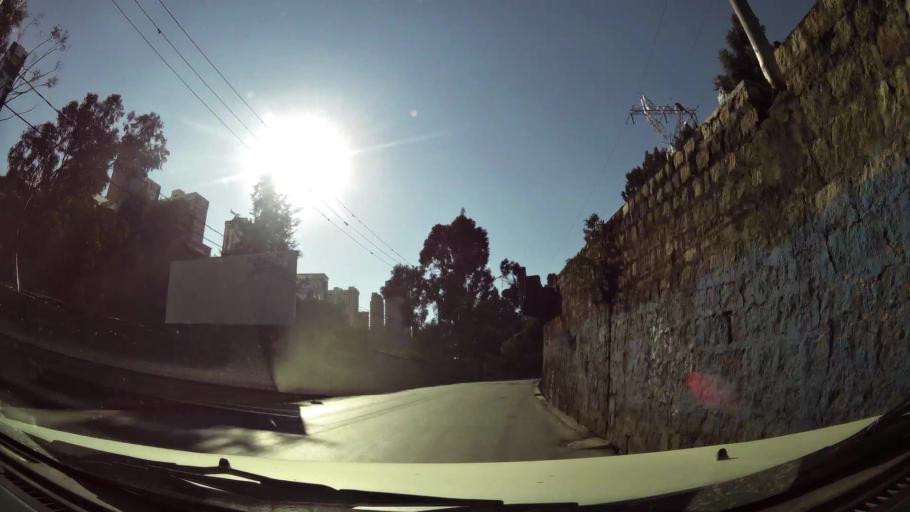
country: BO
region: La Paz
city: La Paz
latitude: -16.5132
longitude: -68.1185
